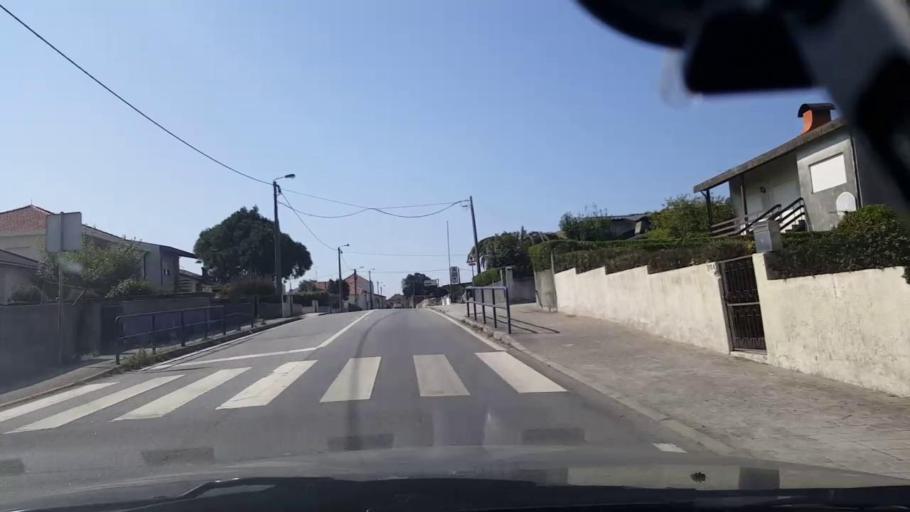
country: PT
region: Porto
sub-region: Povoa de Varzim
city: Pedroso
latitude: 41.3899
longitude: -8.7039
